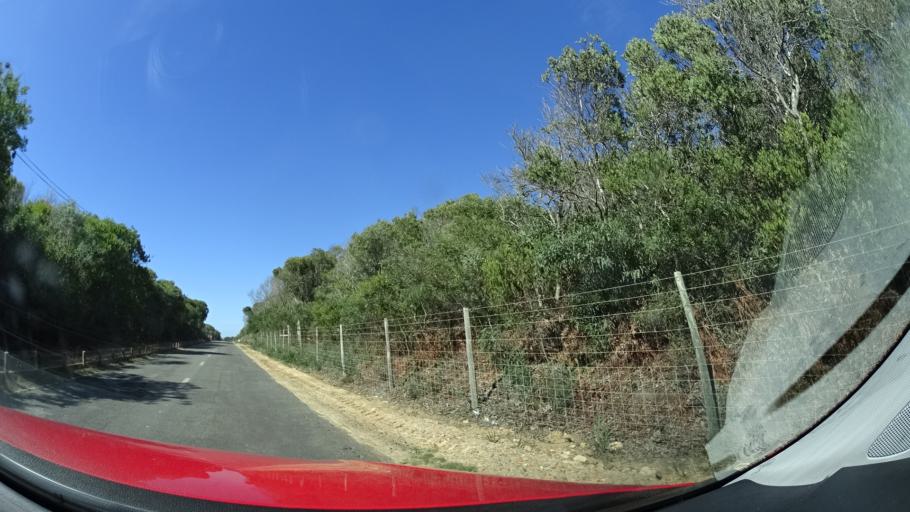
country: PT
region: Beja
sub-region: Odemira
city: Sao Teotonio
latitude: 37.5399
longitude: -8.7864
